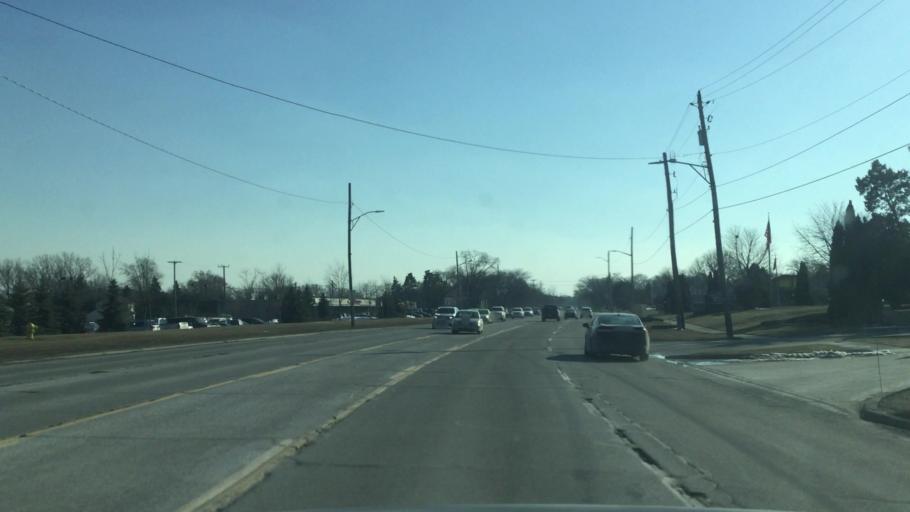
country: US
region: Michigan
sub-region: Wayne County
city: Westland
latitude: 42.3351
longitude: -83.3851
